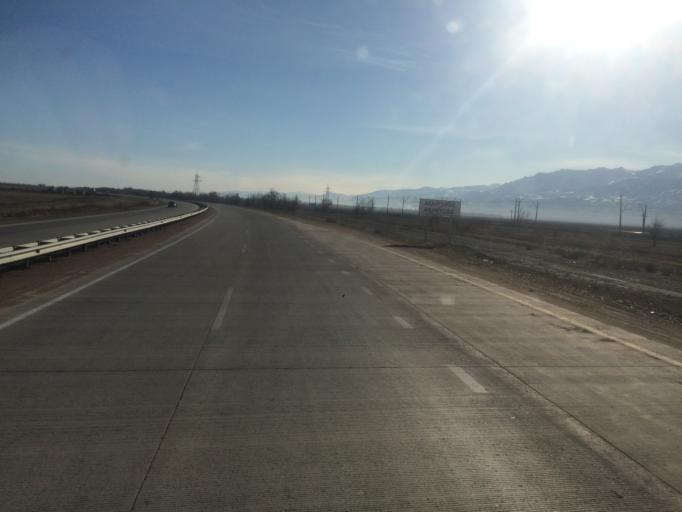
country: KG
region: Talas
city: Ivanovo-Alekseyevka
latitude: 42.9900
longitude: 72.1166
